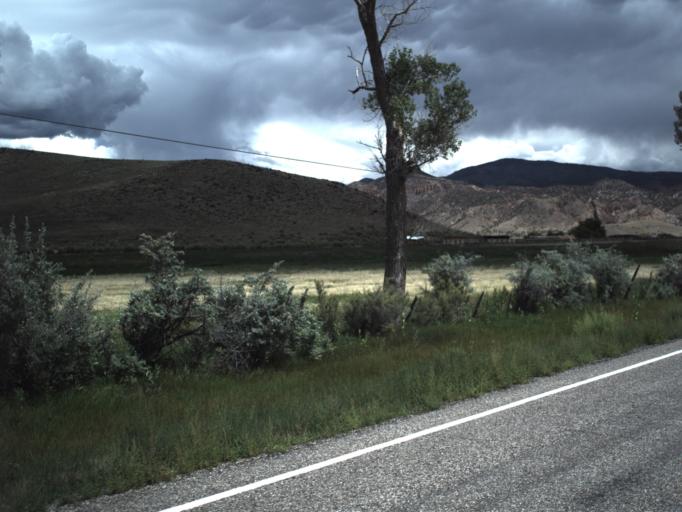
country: US
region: Utah
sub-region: Piute County
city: Junction
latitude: 38.2084
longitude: -112.2021
